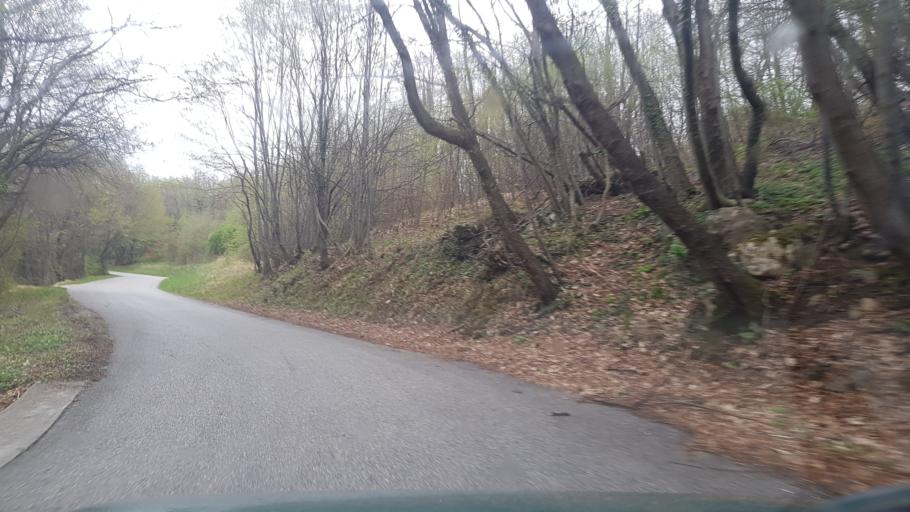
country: SI
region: Kanal
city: Deskle
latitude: 46.0479
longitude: 13.5648
